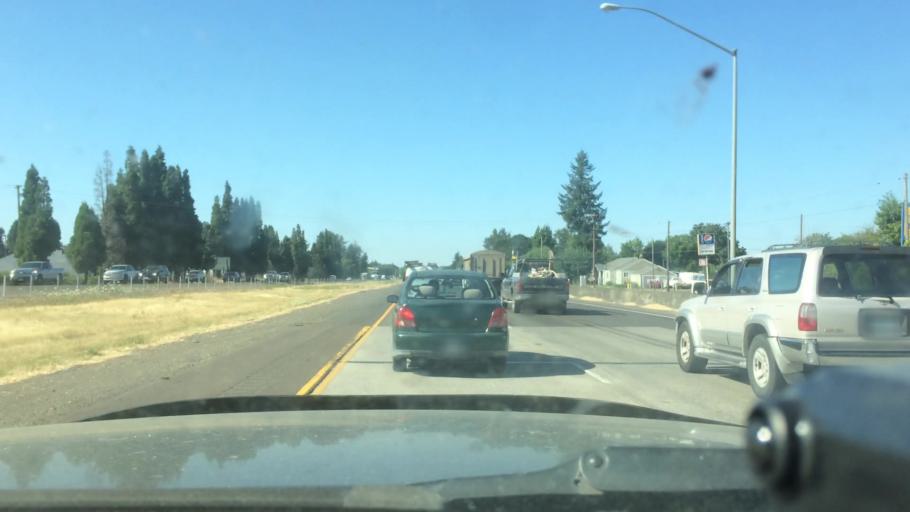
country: US
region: Oregon
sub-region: Linn County
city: Millersburg
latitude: 44.6514
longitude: -123.0614
